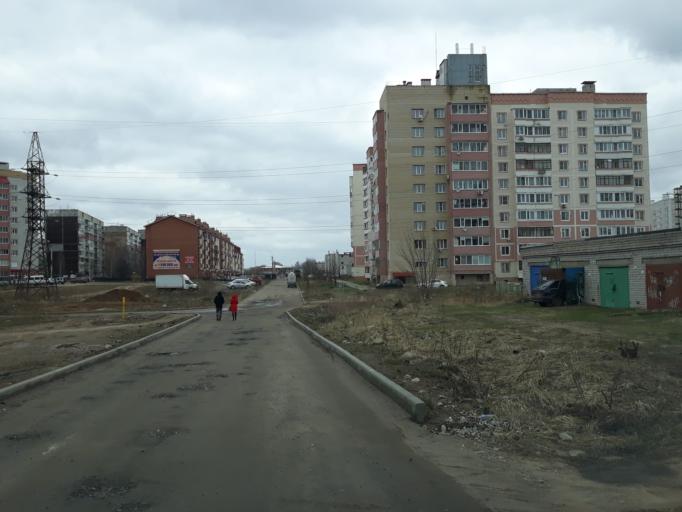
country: RU
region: Jaroslavl
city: Yaroslavl
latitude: 57.6487
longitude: 39.9696
